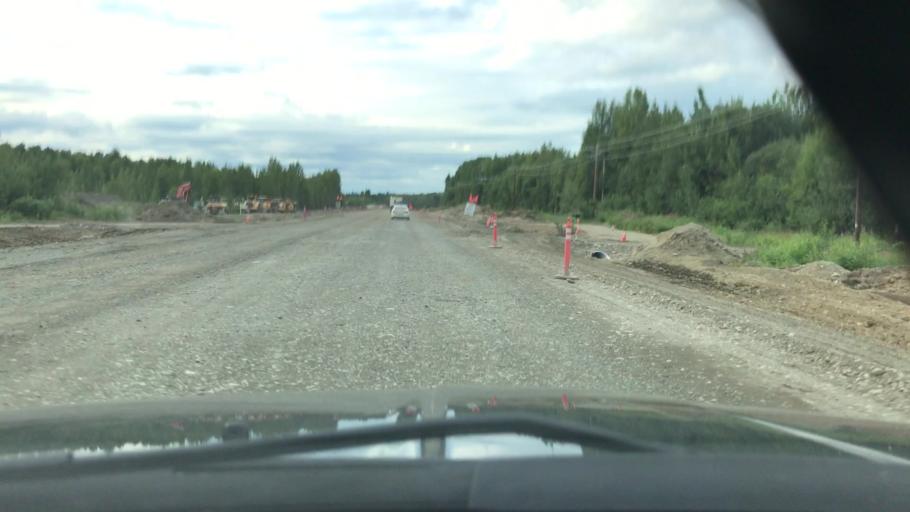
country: US
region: Alaska
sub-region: Matanuska-Susitna Borough
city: Y
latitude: 62.0899
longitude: -150.0614
